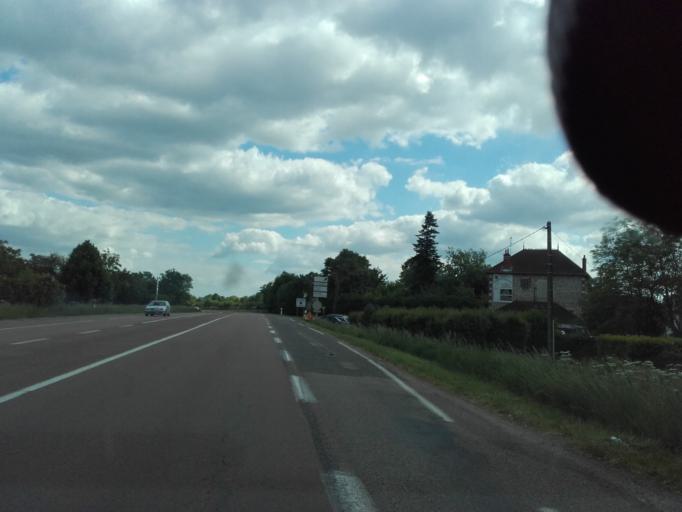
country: FR
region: Bourgogne
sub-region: Departement de Saone-et-Loire
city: Chagny
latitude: 46.9017
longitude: 4.7599
